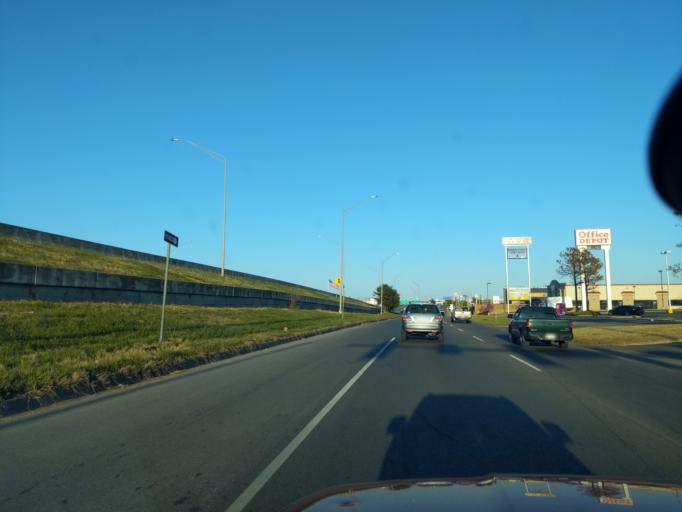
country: US
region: Oklahoma
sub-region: Cleveland County
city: Moore
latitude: 35.3911
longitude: -97.5296
